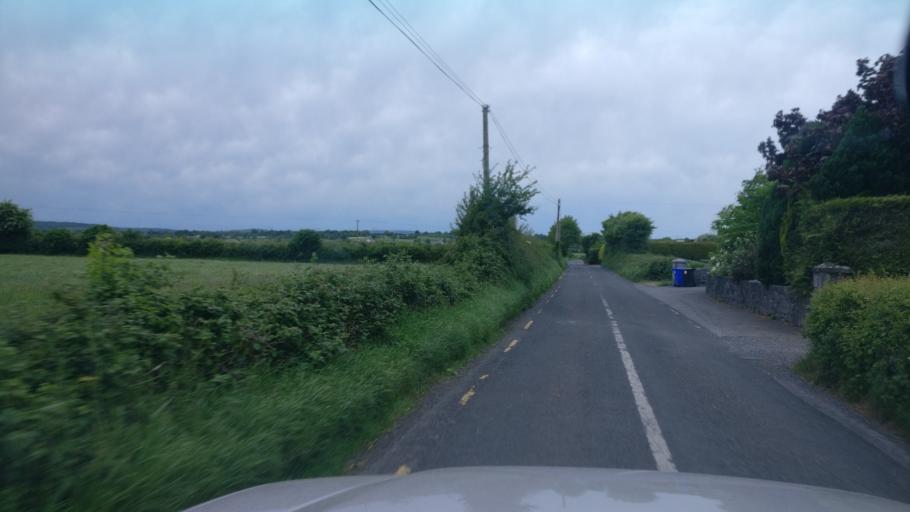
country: IE
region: Connaught
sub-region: County Galway
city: Portumna
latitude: 53.1133
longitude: -8.2928
